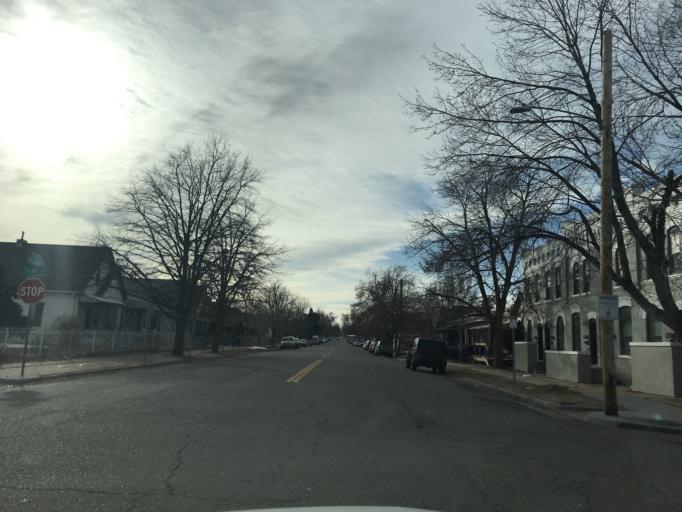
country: US
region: Colorado
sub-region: Denver County
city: Denver
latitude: 39.7670
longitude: -104.9660
